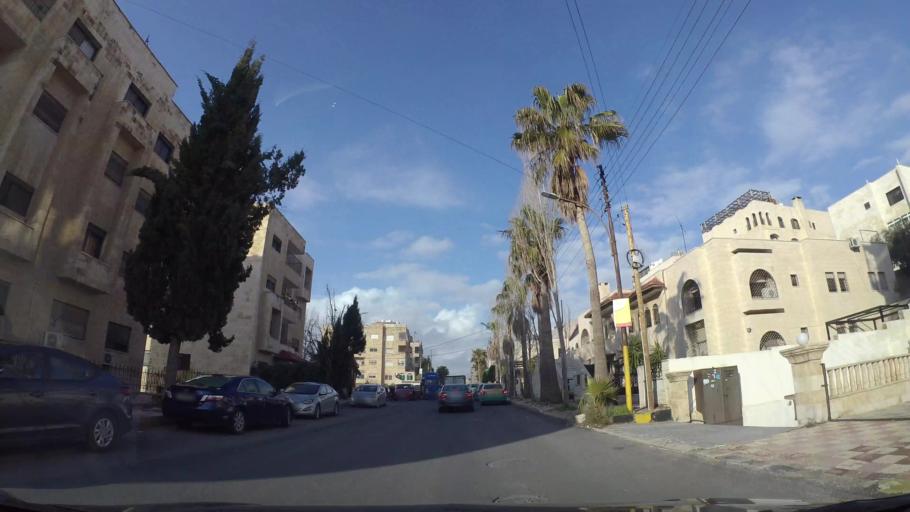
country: JO
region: Amman
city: Al Jubayhah
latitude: 31.9852
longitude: 35.8700
